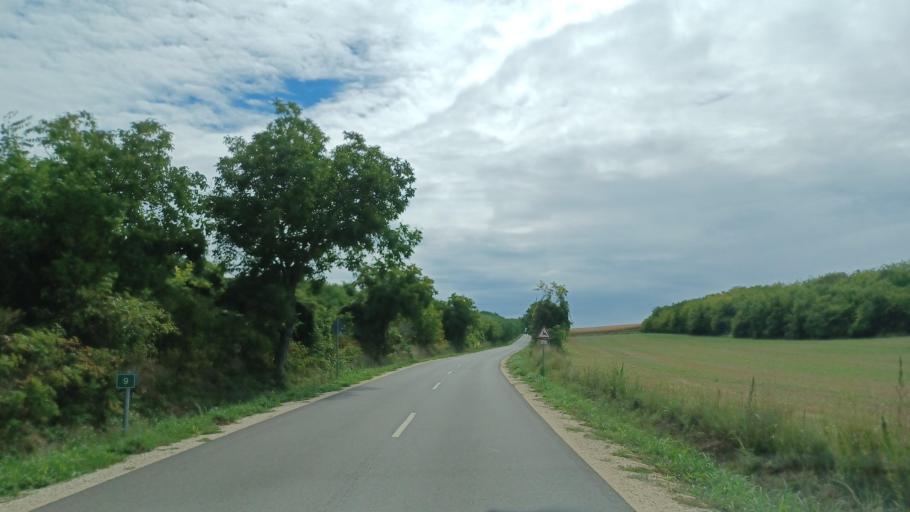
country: HU
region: Tolna
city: Zomba
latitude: 46.4784
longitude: 18.5950
